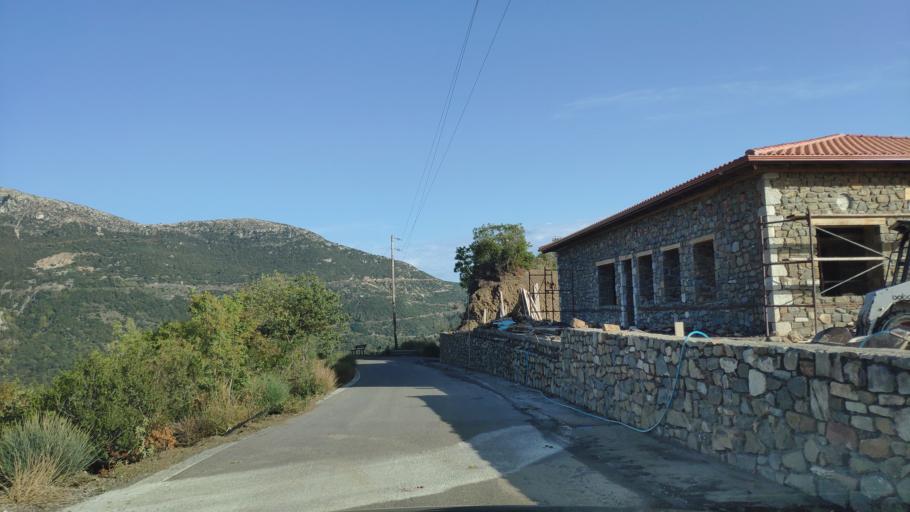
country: GR
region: Peloponnese
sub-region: Nomos Arkadias
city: Dimitsana
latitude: 37.5598
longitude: 22.0350
